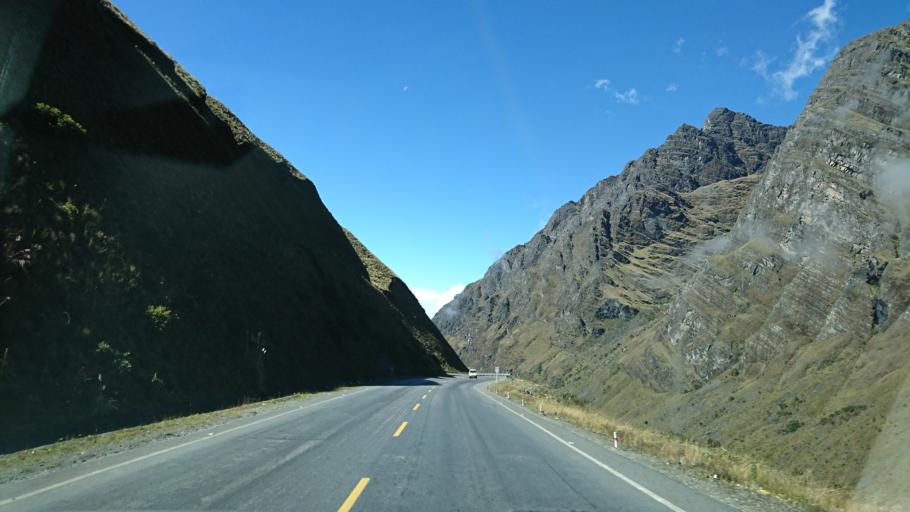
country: BO
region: La Paz
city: Coroico
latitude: -16.3284
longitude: -67.9477
